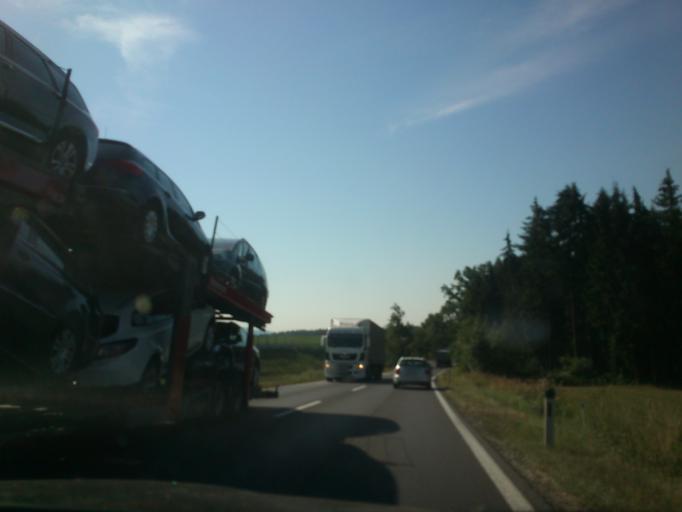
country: AT
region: Upper Austria
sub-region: Politischer Bezirk Freistadt
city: Freistadt
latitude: 48.4759
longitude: 14.4998
